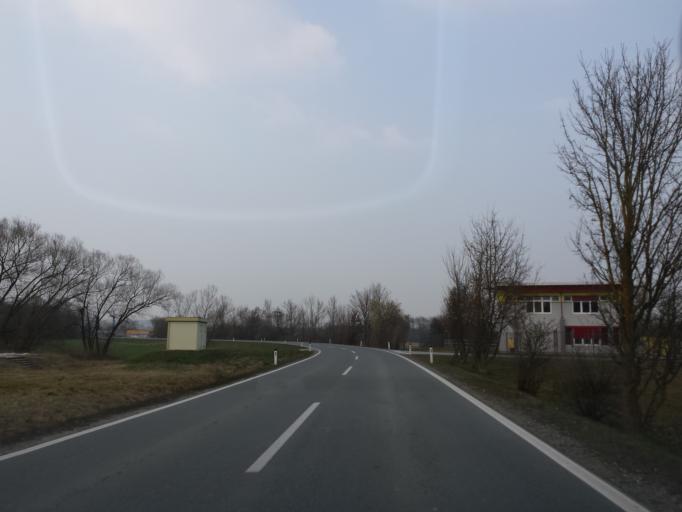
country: AT
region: Styria
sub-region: Politischer Bezirk Hartberg-Fuerstenfeld
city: Fuerstenfeld
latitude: 47.0446
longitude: 16.0989
